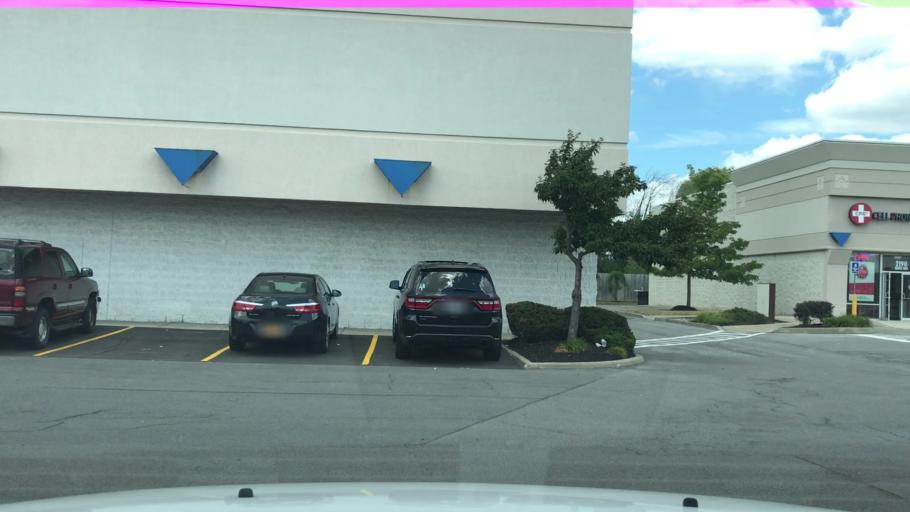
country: US
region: New York
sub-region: Erie County
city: Cheektowaga
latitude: 42.9078
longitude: -78.7558
